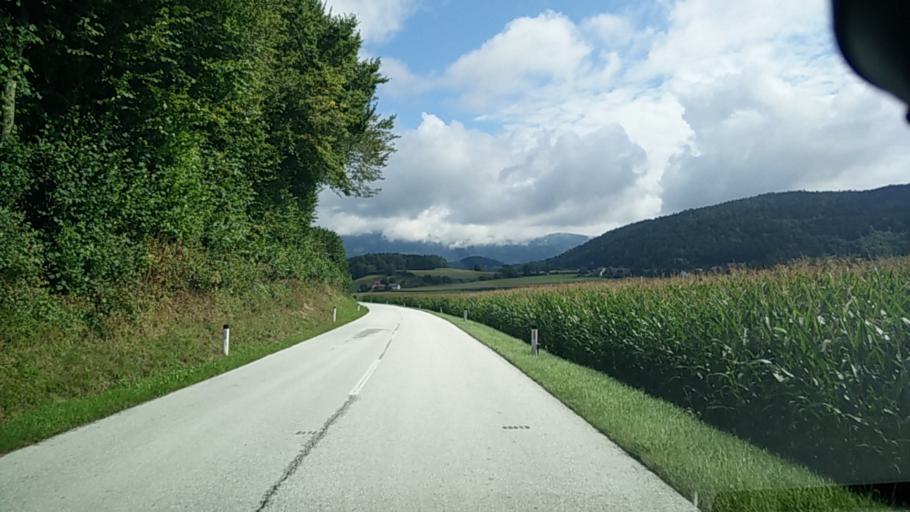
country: AT
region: Carinthia
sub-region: Politischer Bezirk Volkermarkt
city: Voelkermarkt
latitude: 46.6601
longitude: 14.5718
